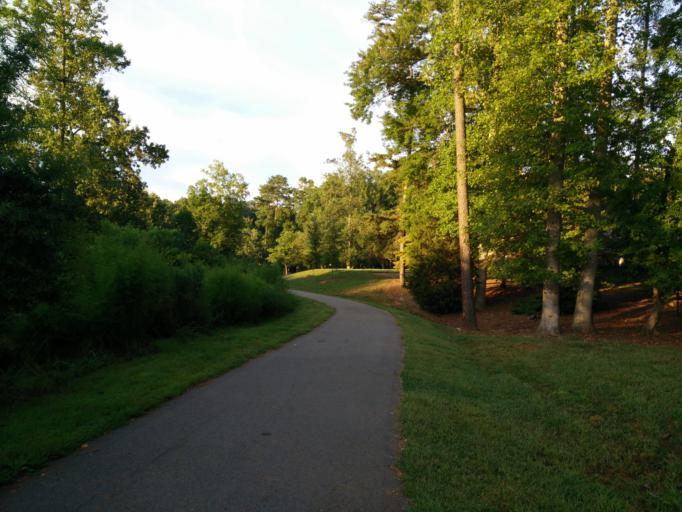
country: US
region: North Carolina
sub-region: Wake County
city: Cary
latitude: 35.7477
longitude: -78.7506
